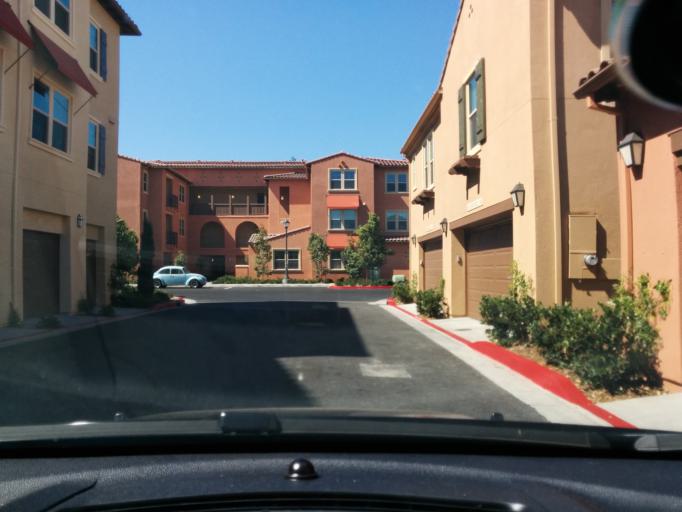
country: US
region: California
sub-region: Santa Clara County
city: Sunnyvale
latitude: 37.3858
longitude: -122.0030
